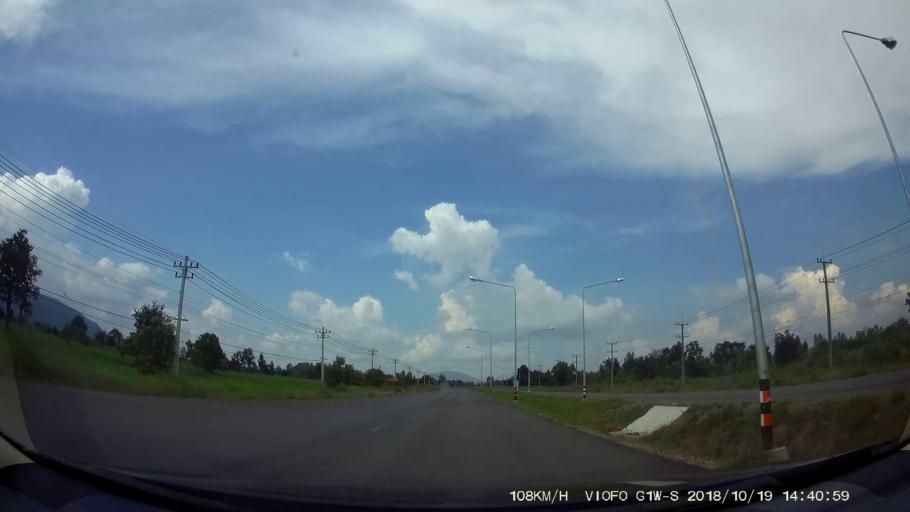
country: TH
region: Chaiyaphum
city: Phu Khiao
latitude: 16.2495
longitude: 102.1976
